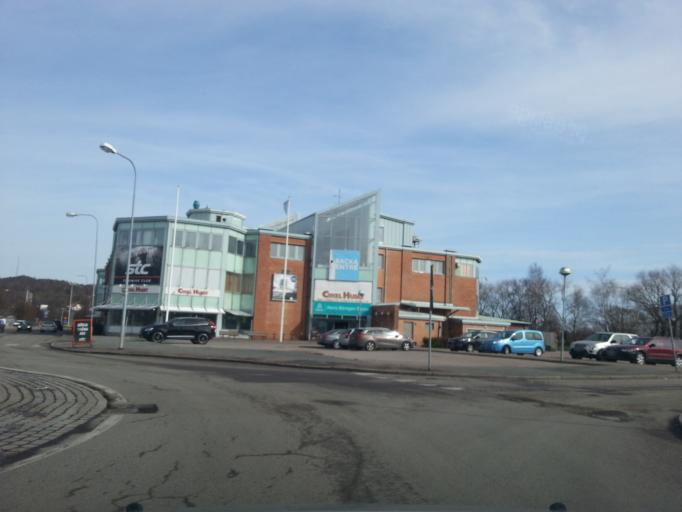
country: SE
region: Vaestra Goetaland
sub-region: Goteborg
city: Goeteborg
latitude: 57.7230
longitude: 11.9572
